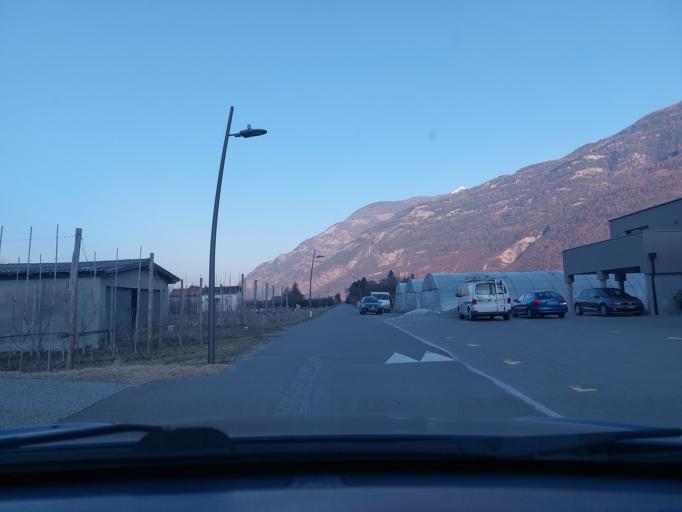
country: CH
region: Valais
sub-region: Martigny District
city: Saxon
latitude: 46.1554
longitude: 7.1780
